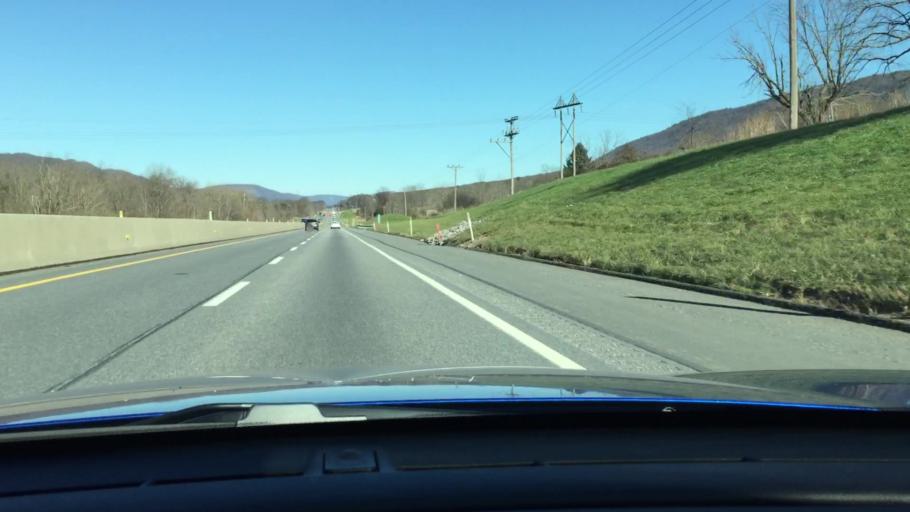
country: US
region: Pennsylvania
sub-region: Franklin County
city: Doylestown
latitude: 40.1311
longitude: -77.7415
